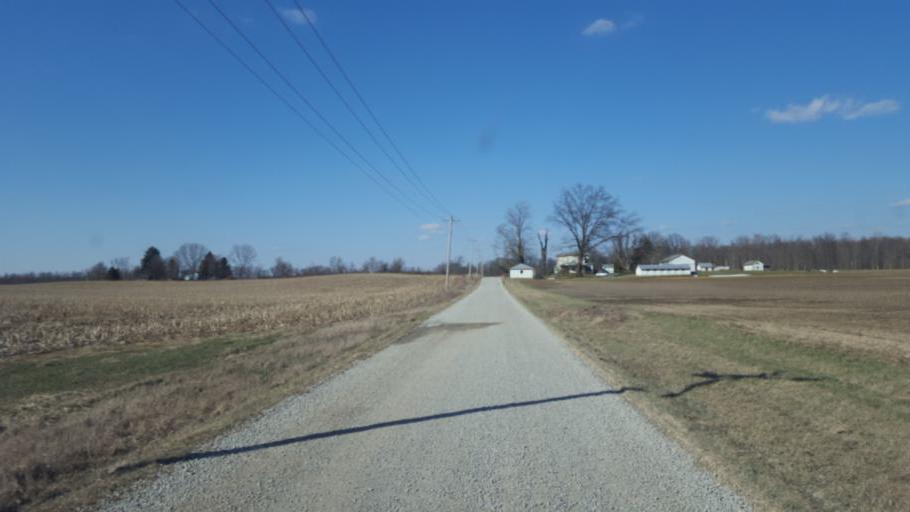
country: US
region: Ohio
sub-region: Morrow County
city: Mount Gilead
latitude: 40.5036
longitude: -82.7717
